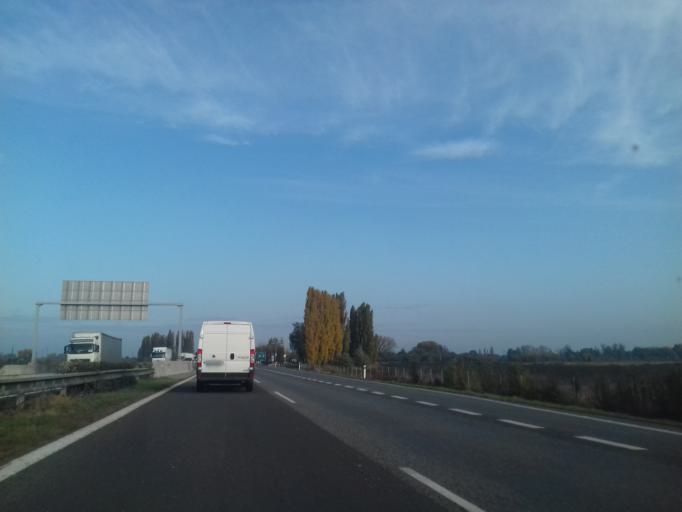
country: SK
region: Bratislavsky
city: Stupava
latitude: 48.2570
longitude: 17.0107
